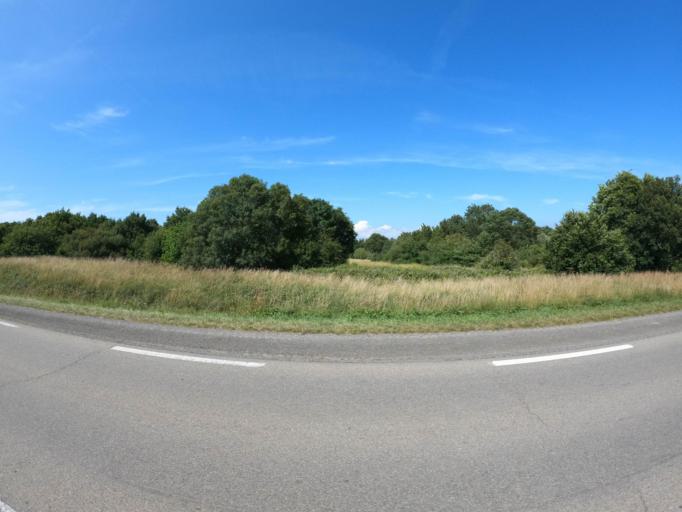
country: FR
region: Pays de la Loire
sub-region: Departement de la Loire-Atlantique
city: Pornic
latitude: 47.1069
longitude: -2.0589
